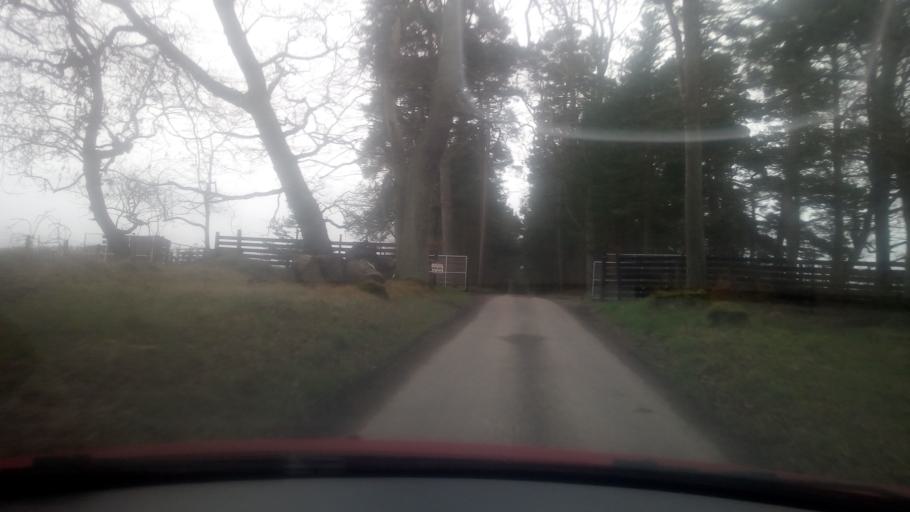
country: GB
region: Scotland
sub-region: The Scottish Borders
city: Jedburgh
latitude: 55.4318
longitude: -2.6408
